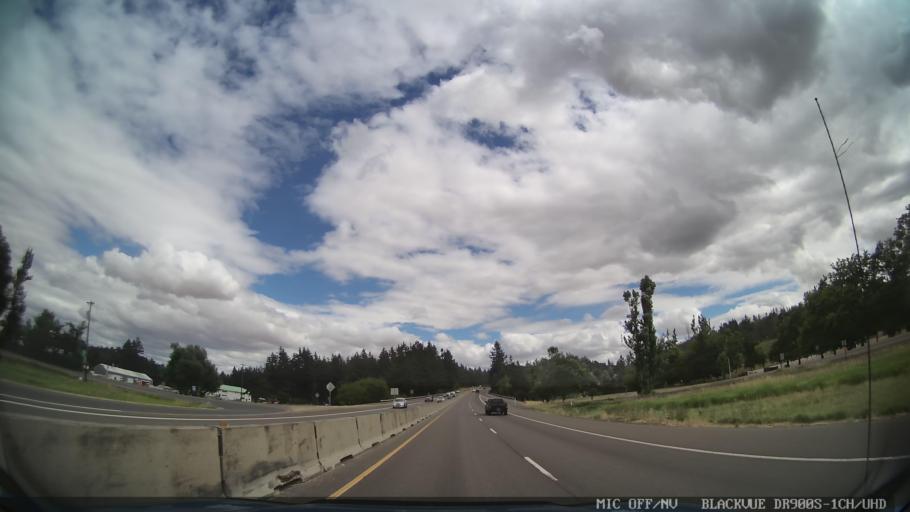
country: US
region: Oregon
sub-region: Marion County
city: Four Corners
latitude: 44.9011
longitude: -122.9436
